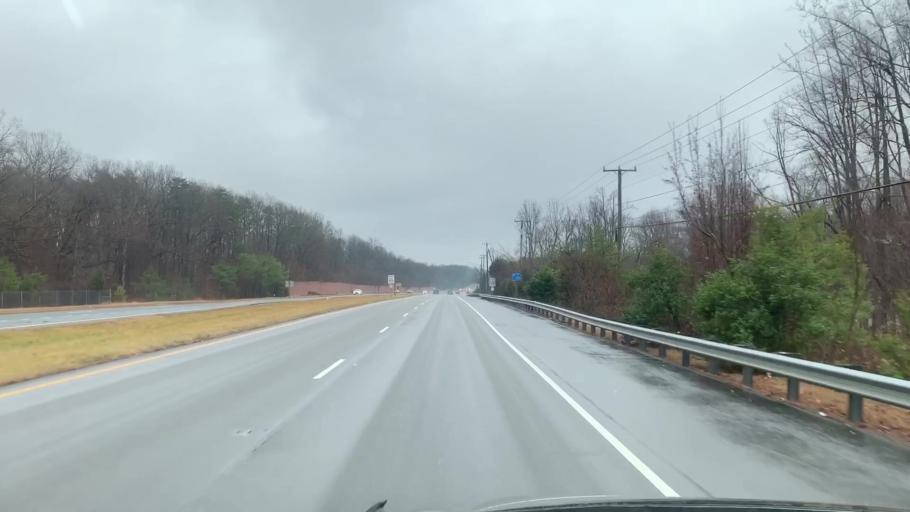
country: US
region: Virginia
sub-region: Fairfax County
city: Burke
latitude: 38.7523
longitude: -77.3003
